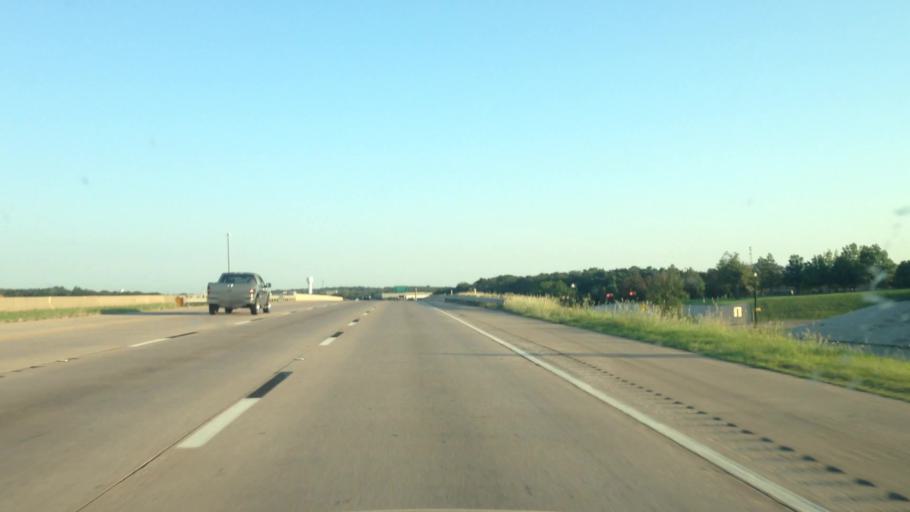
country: US
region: Texas
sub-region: Tarrant County
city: Southlake
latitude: 32.9689
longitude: -97.1579
